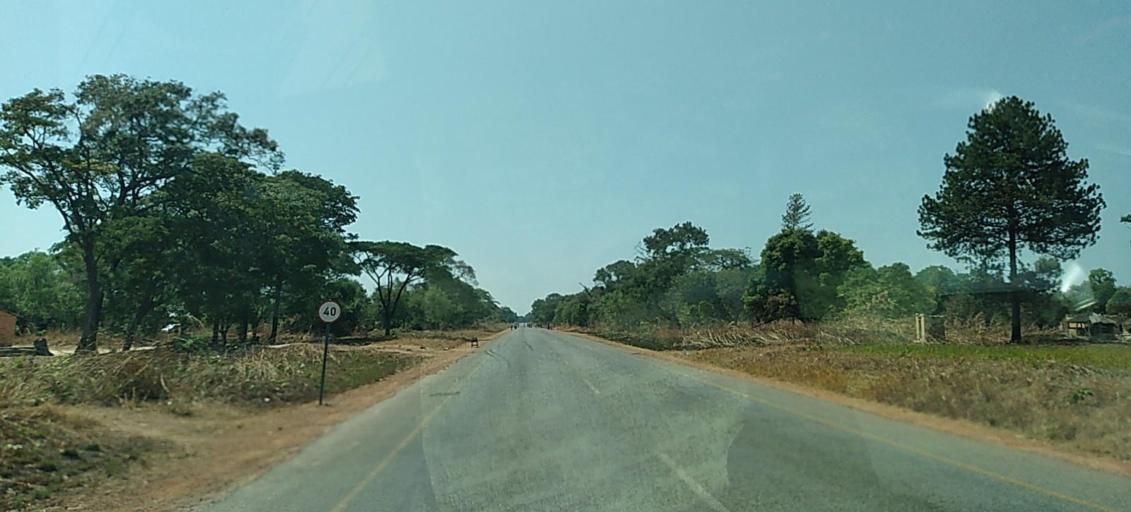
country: ZM
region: North-Western
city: Solwezi
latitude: -12.2884
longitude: 25.6934
